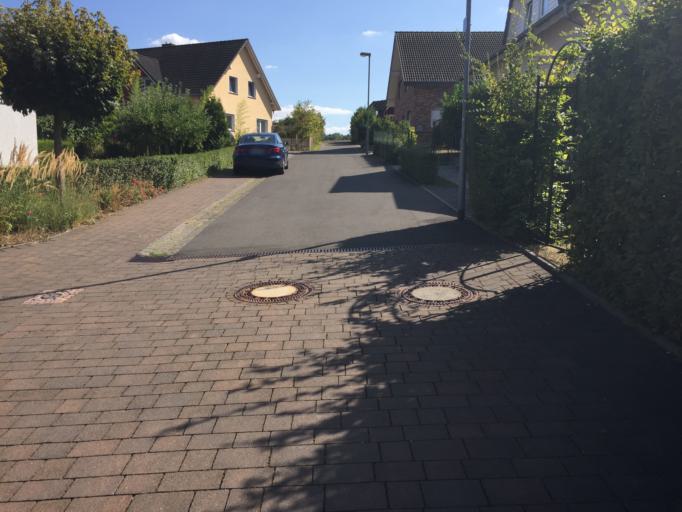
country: DE
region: Hesse
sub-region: Regierungsbezirk Giessen
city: Grunberg
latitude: 50.5956
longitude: 8.9287
